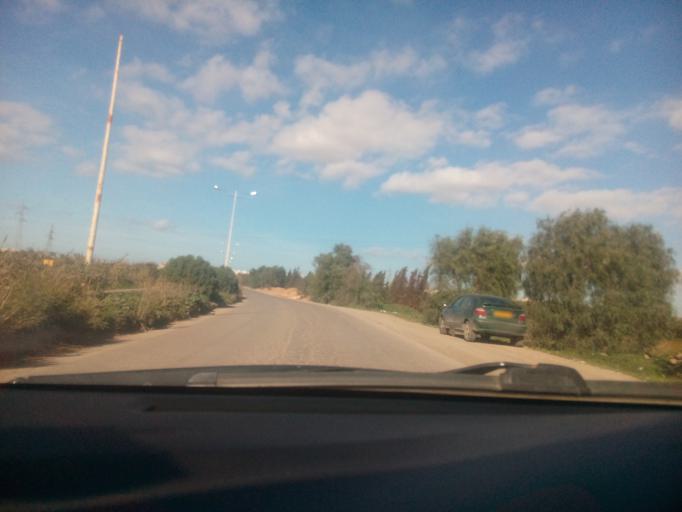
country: DZ
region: Oran
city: Sidi ech Chahmi
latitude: 35.6763
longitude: -0.5657
